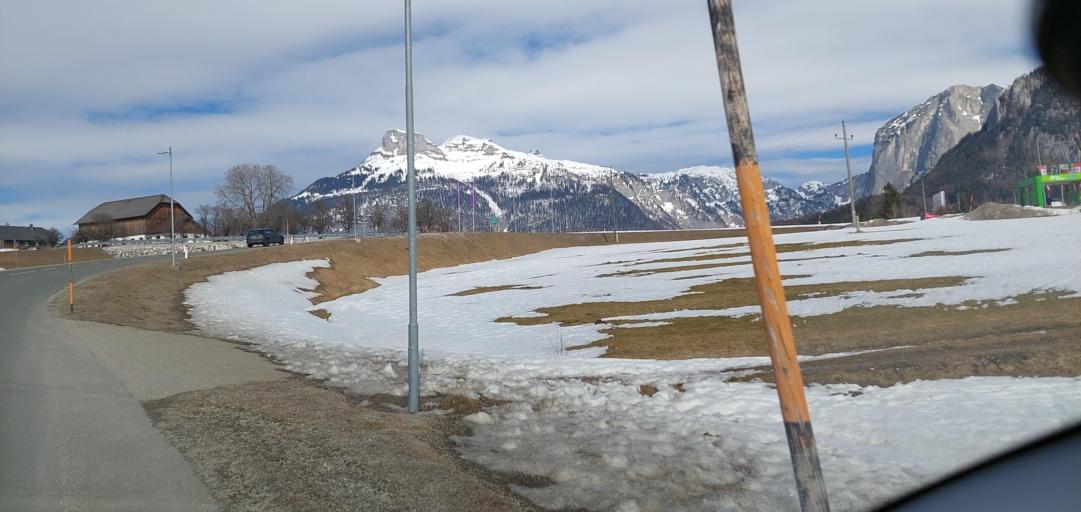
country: AT
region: Styria
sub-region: Politischer Bezirk Liezen
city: Bad Aussee
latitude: 47.6127
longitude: 13.7647
